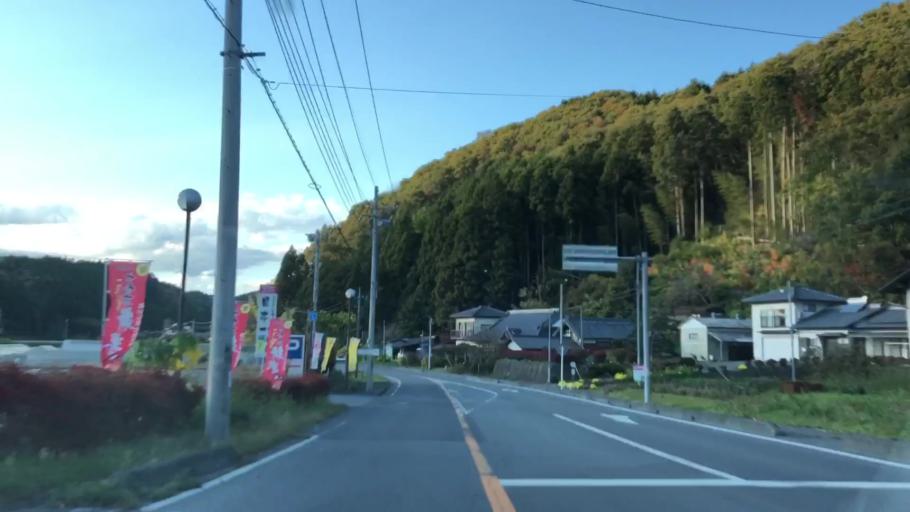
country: JP
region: Ibaraki
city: Kasama
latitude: 36.4780
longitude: 140.3006
